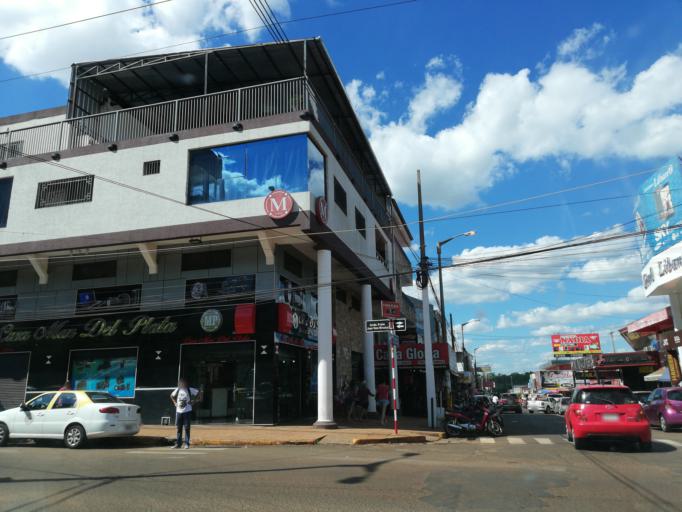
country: PY
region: Itapua
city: Encarnacion
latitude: -27.3594
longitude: -55.8488
